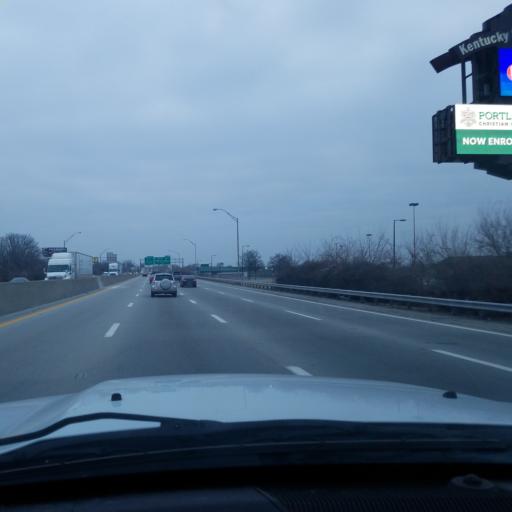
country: US
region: Kentucky
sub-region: Jefferson County
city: Audubon Park
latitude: 38.2050
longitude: -85.7422
